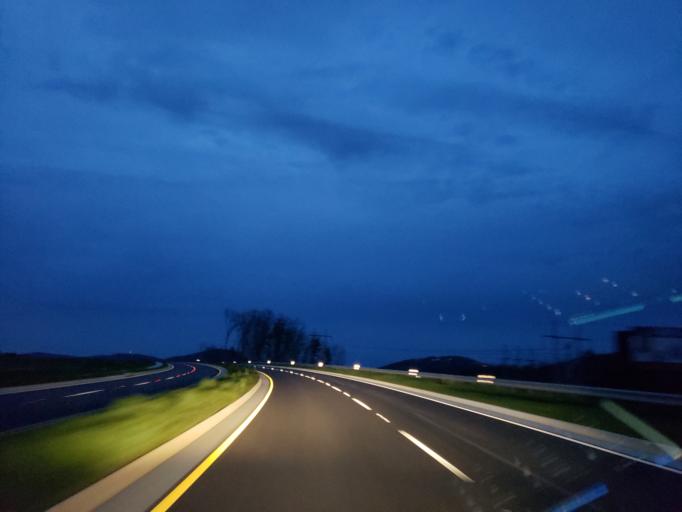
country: US
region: Georgia
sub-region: Bartow County
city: Emerson
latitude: 34.1311
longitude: -84.7400
